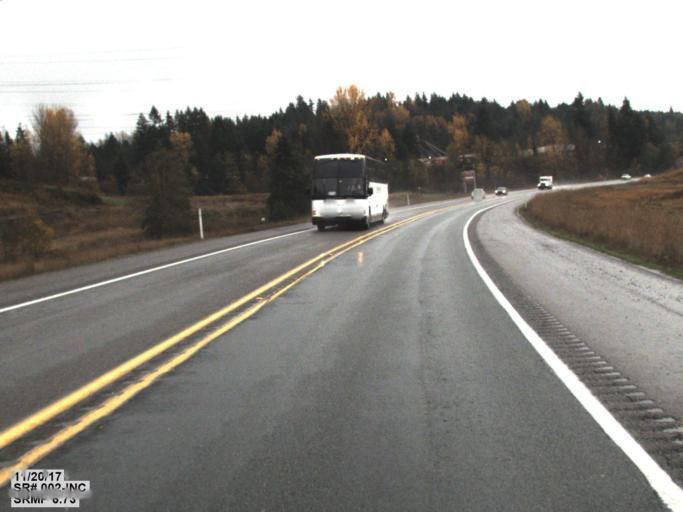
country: US
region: Washington
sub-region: Snohomish County
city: Snohomish
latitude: 47.9404
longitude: -122.0706
